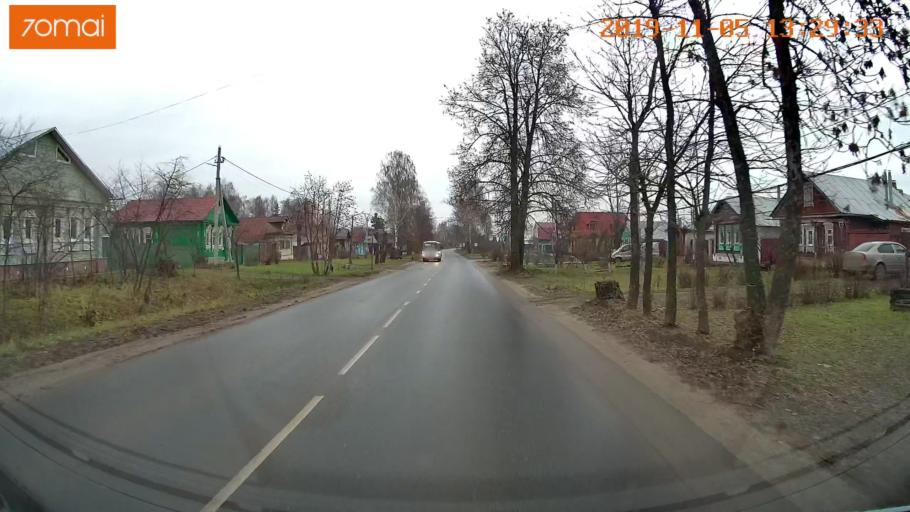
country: RU
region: Ivanovo
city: Shuya
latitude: 56.8614
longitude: 41.3975
